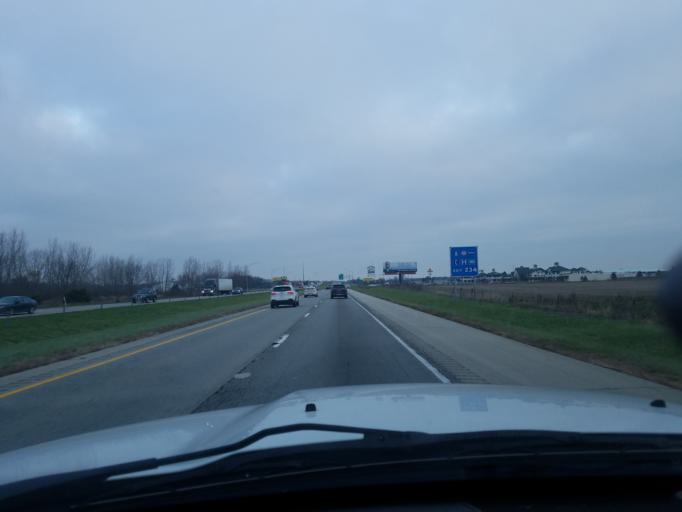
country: US
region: Indiana
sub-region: Delaware County
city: Daleville
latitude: 40.1046
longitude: -85.5688
